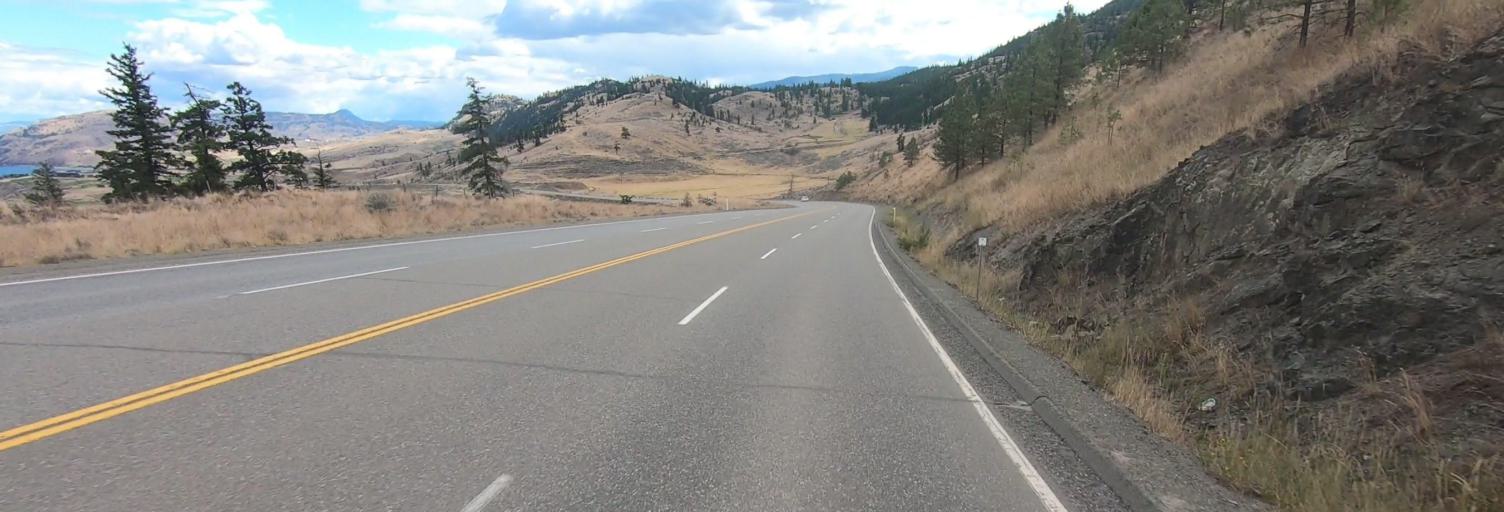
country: CA
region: British Columbia
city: Logan Lake
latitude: 50.7481
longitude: -120.7188
